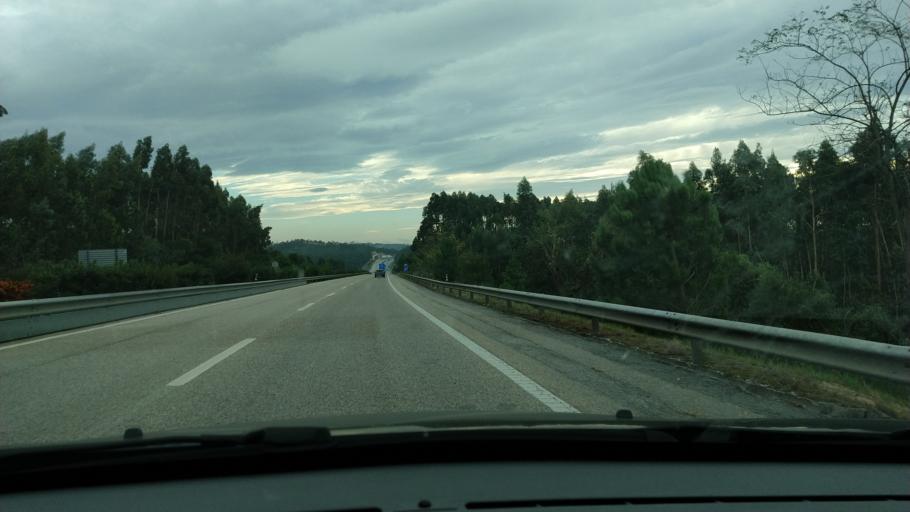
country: PT
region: Coimbra
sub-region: Figueira da Foz
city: Alhadas
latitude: 40.1536
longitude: -8.8026
